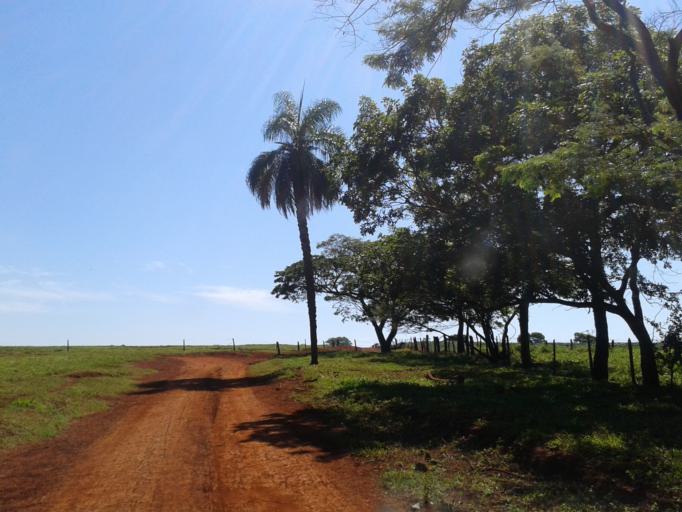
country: BR
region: Minas Gerais
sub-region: Centralina
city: Centralina
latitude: -18.6334
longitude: -49.2956
